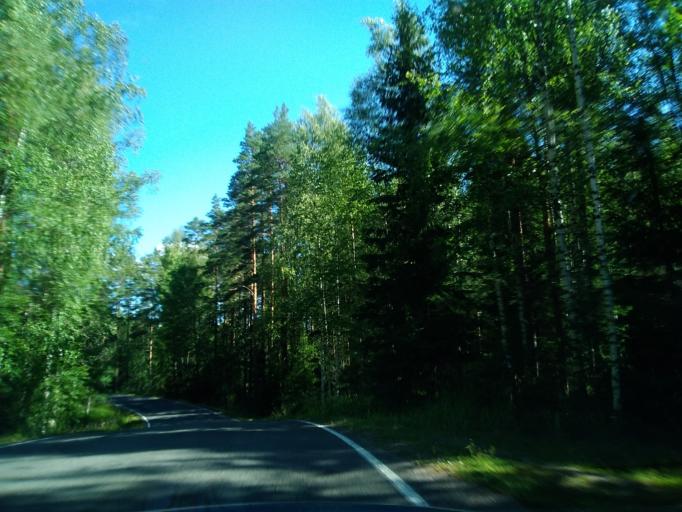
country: FI
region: Uusimaa
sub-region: Helsinki
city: Kaerkoelae
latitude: 60.7847
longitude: 24.0807
